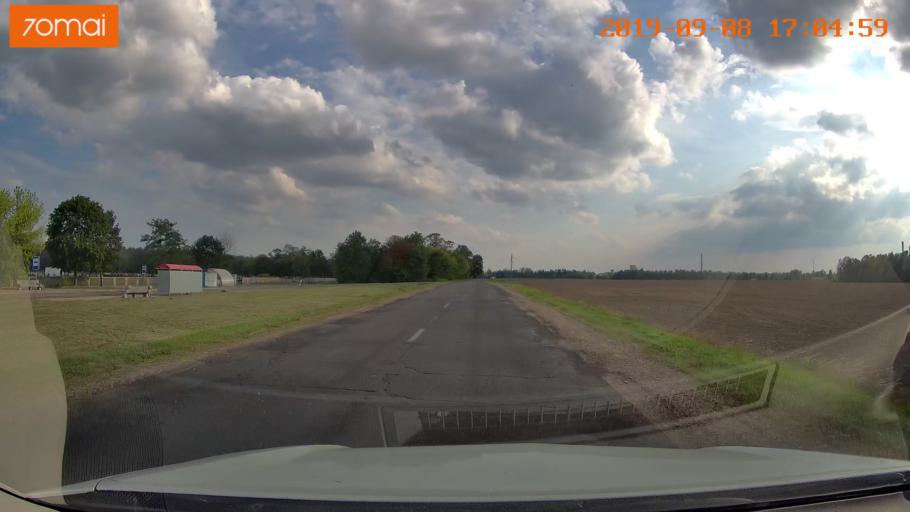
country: BY
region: Grodnenskaya
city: Hrodna
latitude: 53.6838
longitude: 23.9558
